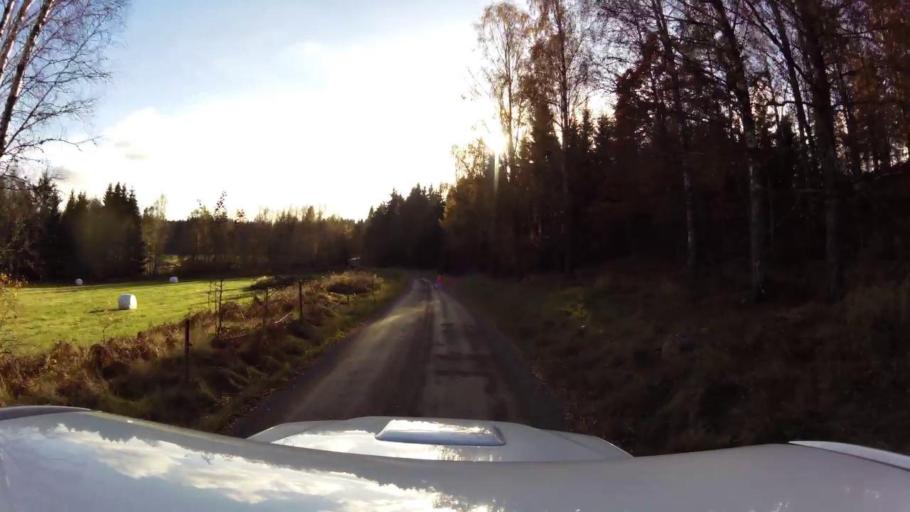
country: SE
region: OEstergoetland
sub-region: Linkopings Kommun
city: Vikingstad
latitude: 58.2165
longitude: 15.4407
